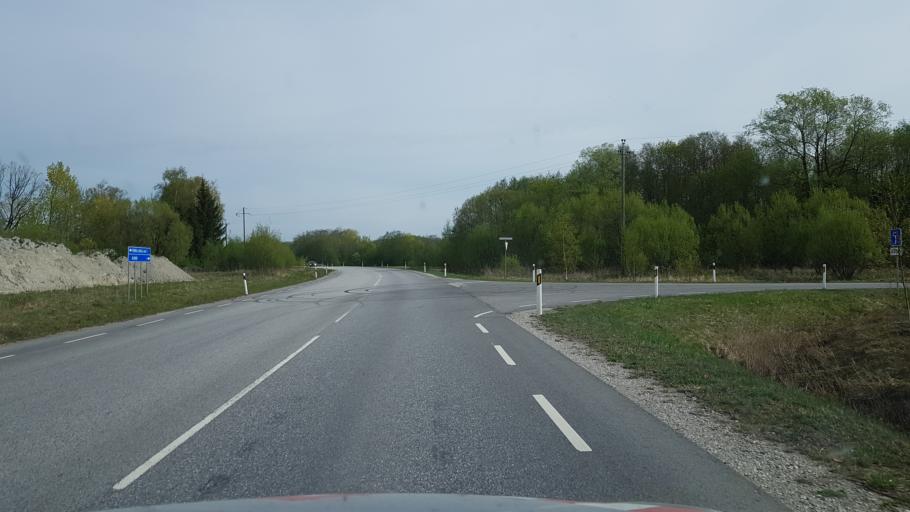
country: EE
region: Paernumaa
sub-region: Sauga vald
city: Sauga
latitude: 58.4117
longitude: 24.4402
